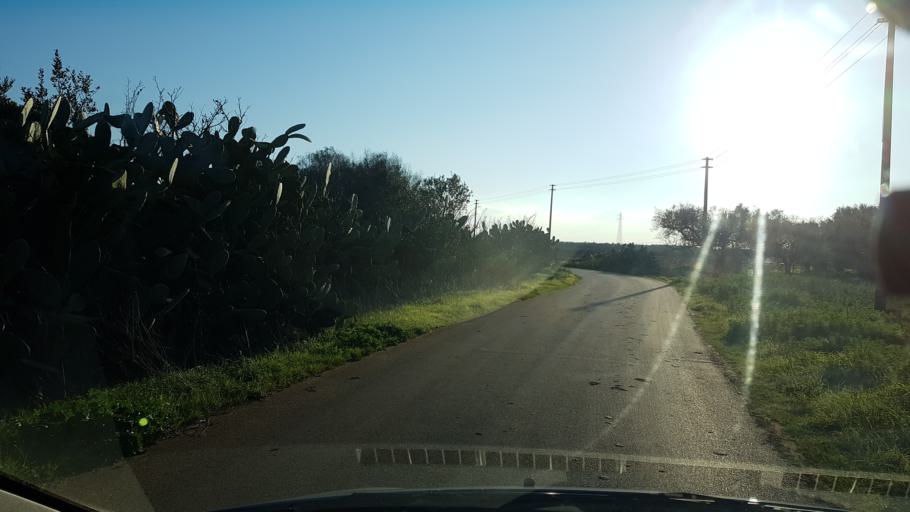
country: IT
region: Apulia
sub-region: Provincia di Brindisi
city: Mesagne
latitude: 40.5715
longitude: 17.8716
